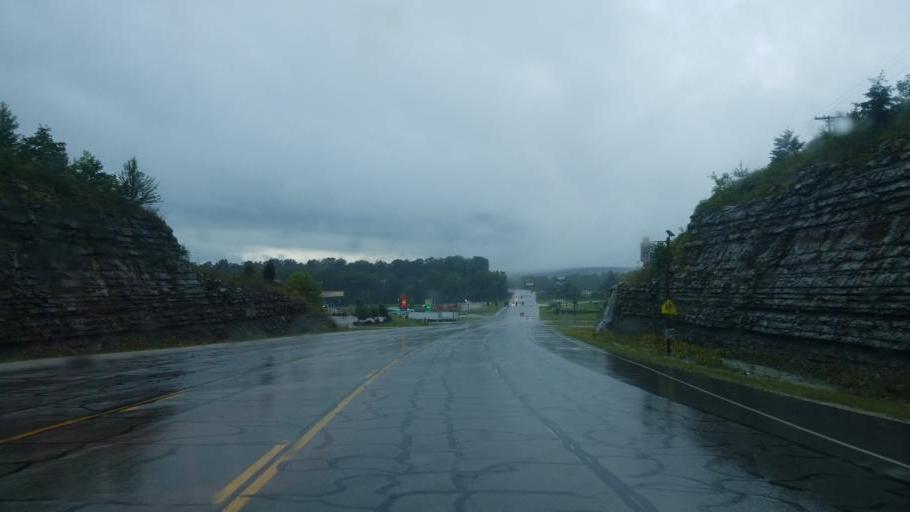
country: US
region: Kentucky
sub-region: Rowan County
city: Morehead
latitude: 38.2026
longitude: -83.4744
